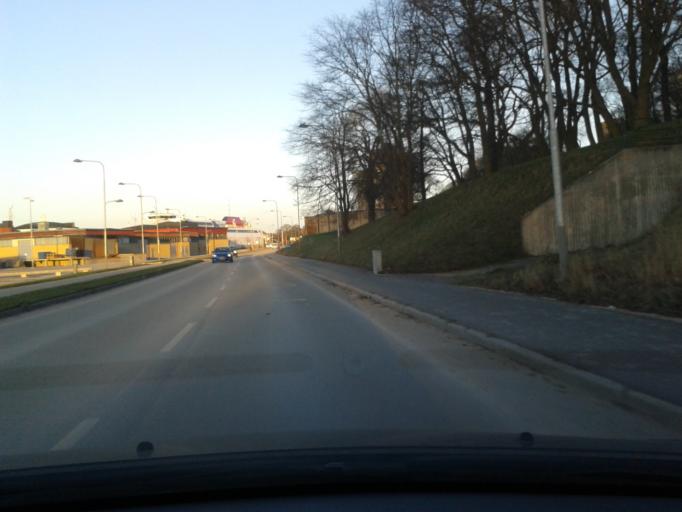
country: SE
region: Gotland
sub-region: Gotland
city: Visby
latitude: 57.6349
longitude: 18.2838
